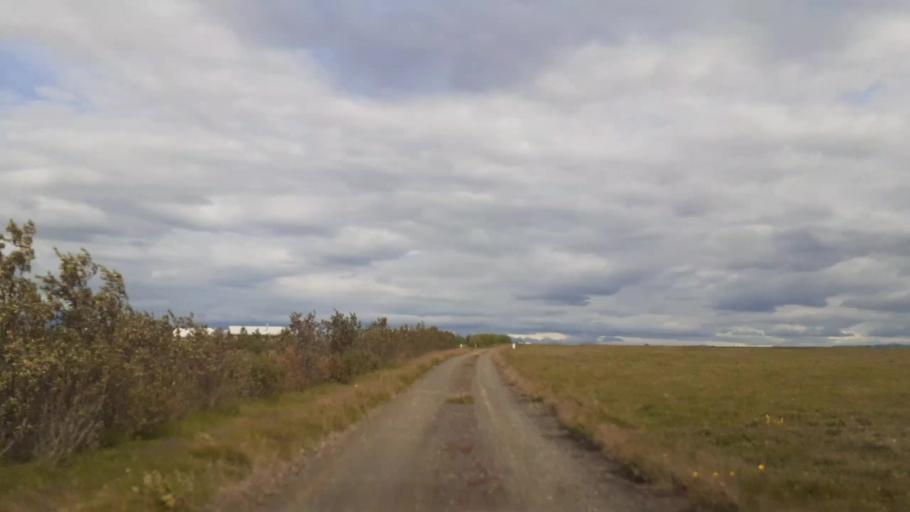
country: IS
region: South
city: Vestmannaeyjar
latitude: 63.7722
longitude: -20.2982
